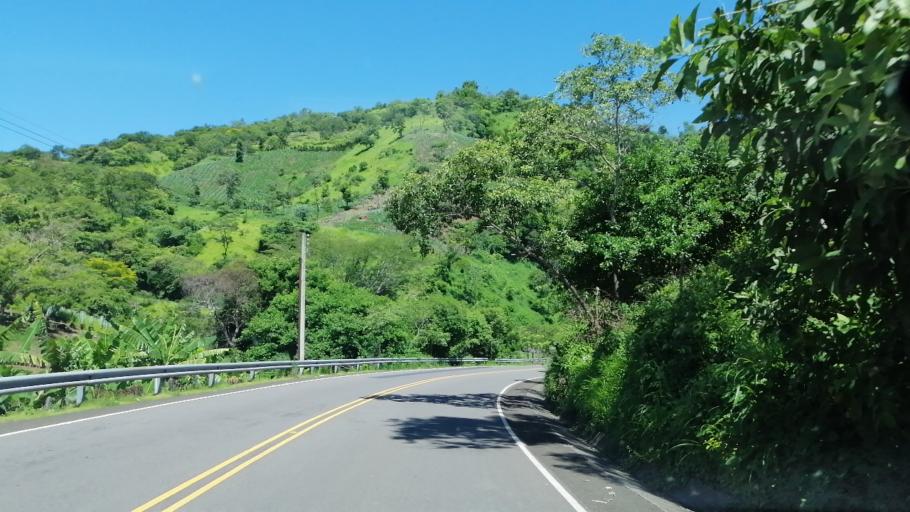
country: SV
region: San Miguel
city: Ciudad Barrios
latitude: 13.8132
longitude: -88.1784
